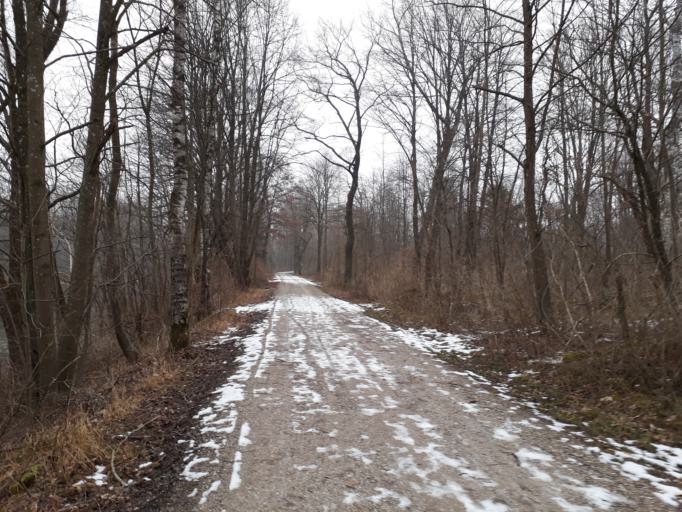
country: DE
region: Bavaria
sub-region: Upper Bavaria
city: Unterfoehring
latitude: 48.2162
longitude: 11.6519
